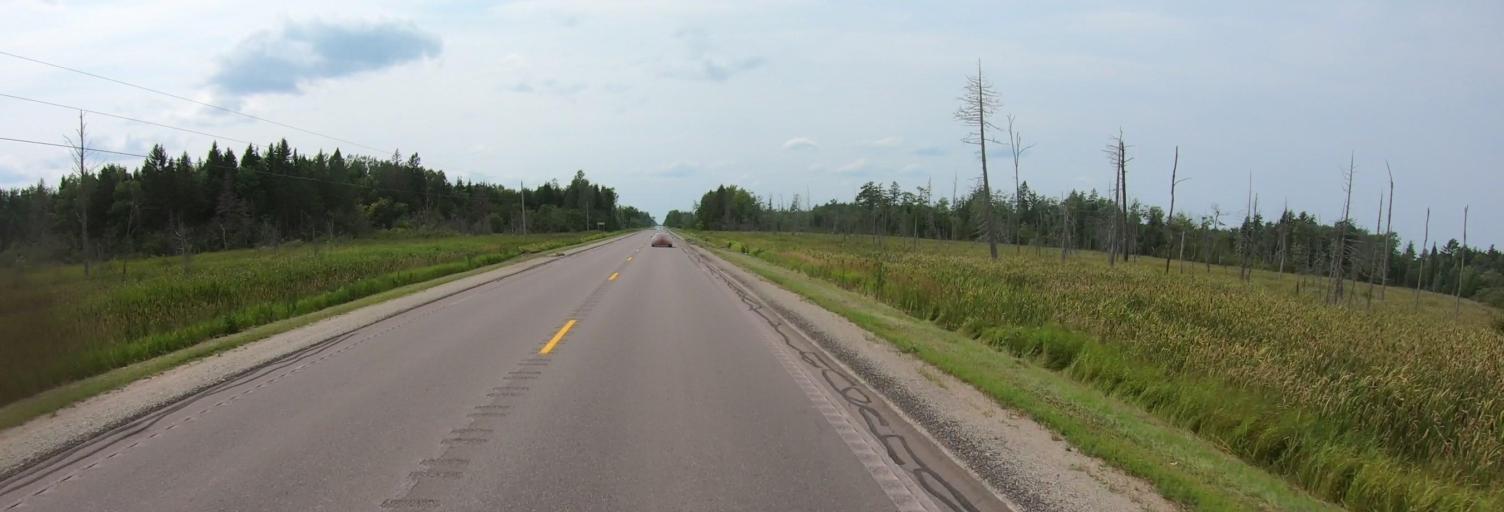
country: US
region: Michigan
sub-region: Marquette County
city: K. I. Sawyer Air Force Base
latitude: 46.3476
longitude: -87.1595
